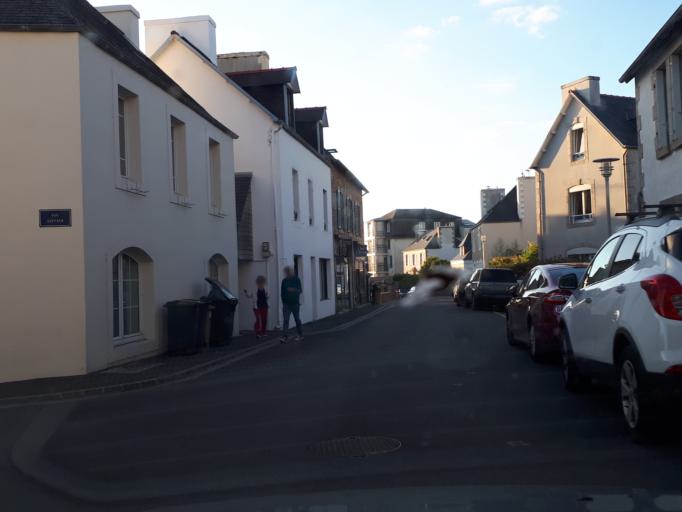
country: FR
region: Brittany
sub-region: Departement du Finistere
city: Carantec
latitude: 48.6694
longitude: -3.9153
